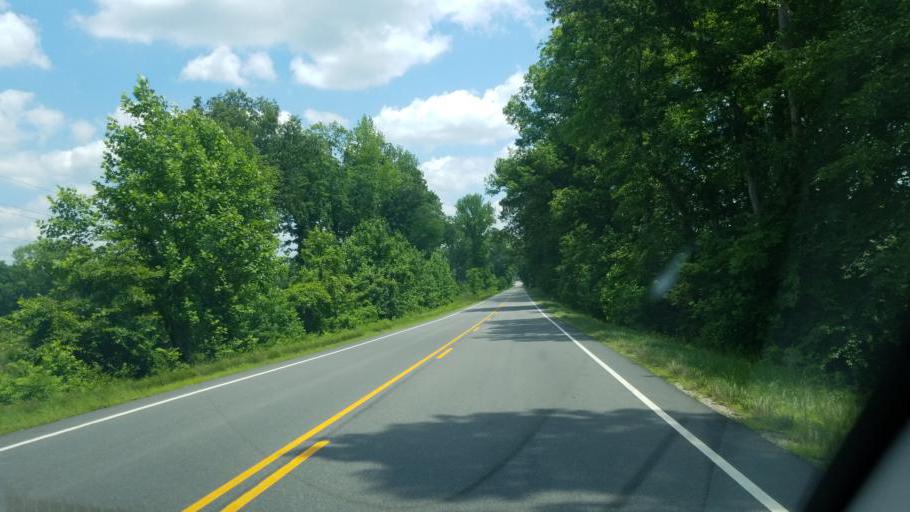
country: US
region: Virginia
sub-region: Cumberland County
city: Cumberland
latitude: 37.4869
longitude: -78.3307
